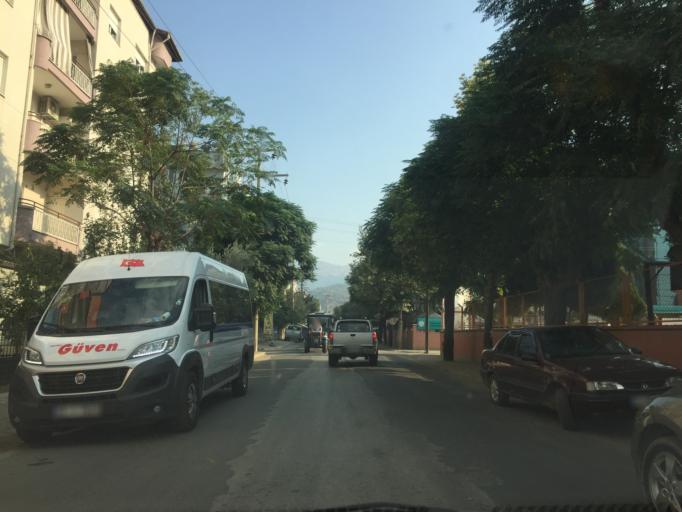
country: TR
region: Manisa
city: Salihli
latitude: 38.4890
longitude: 28.1513
